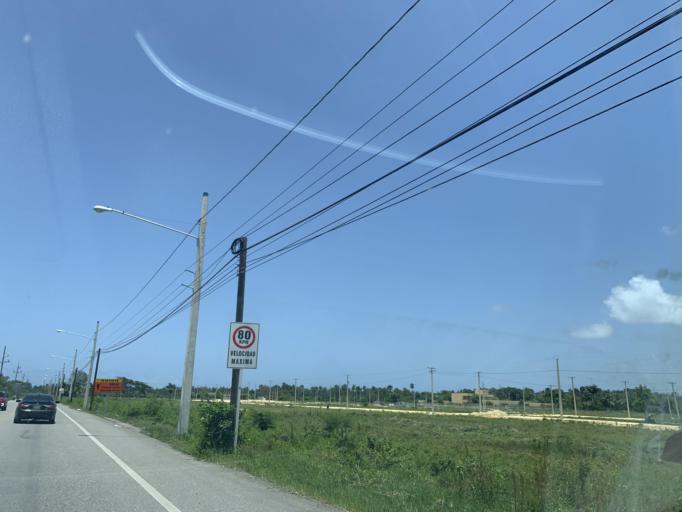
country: DO
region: Puerto Plata
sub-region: Puerto Plata
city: Puerto Plata
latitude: 19.7407
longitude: -70.6017
